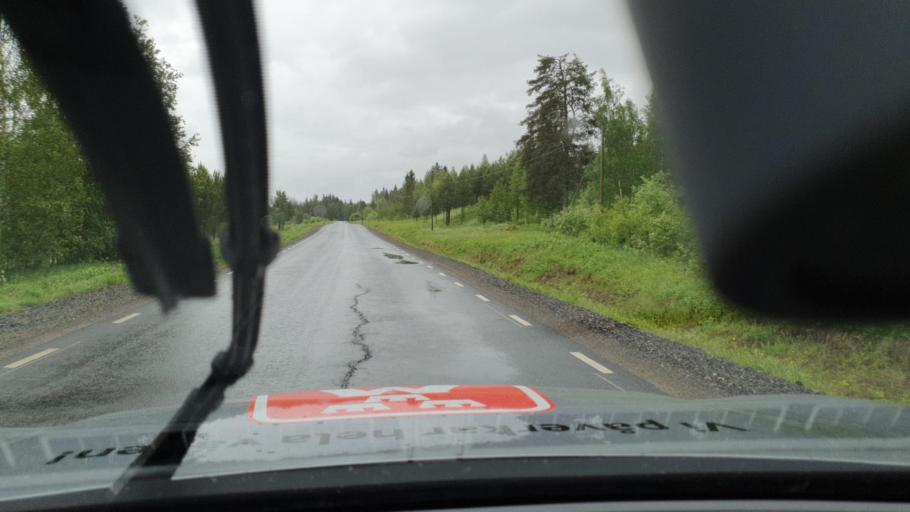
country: FI
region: Lapland
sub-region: Torniolaakso
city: Ylitornio
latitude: 66.2088
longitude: 23.6956
